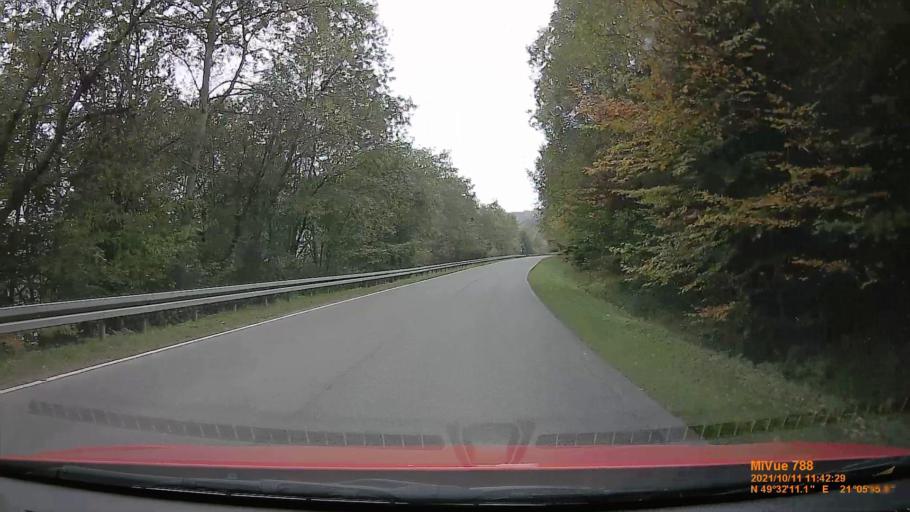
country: PL
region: Lesser Poland Voivodeship
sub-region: Powiat gorlicki
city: Uscie Gorlickie
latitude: 49.5363
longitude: 21.0991
